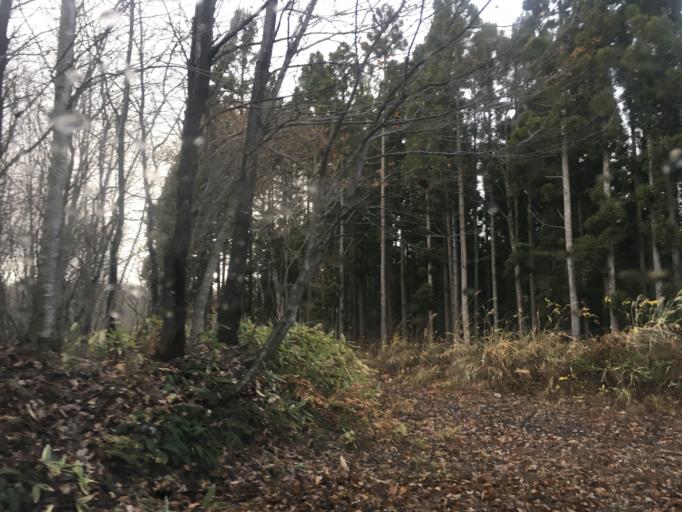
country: JP
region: Iwate
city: Ichinoseki
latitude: 38.9775
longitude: 140.9440
